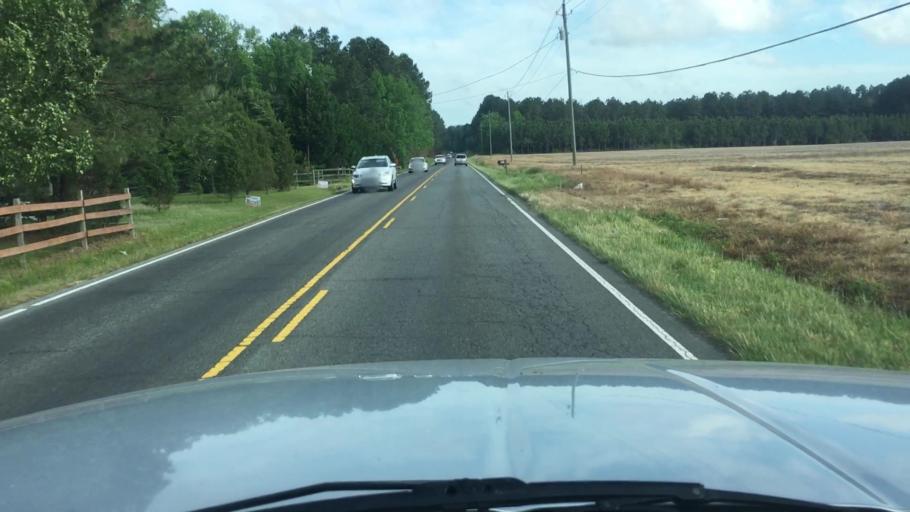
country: US
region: North Carolina
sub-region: Johnston County
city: Wilsons Mills
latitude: 35.6253
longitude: -78.3284
